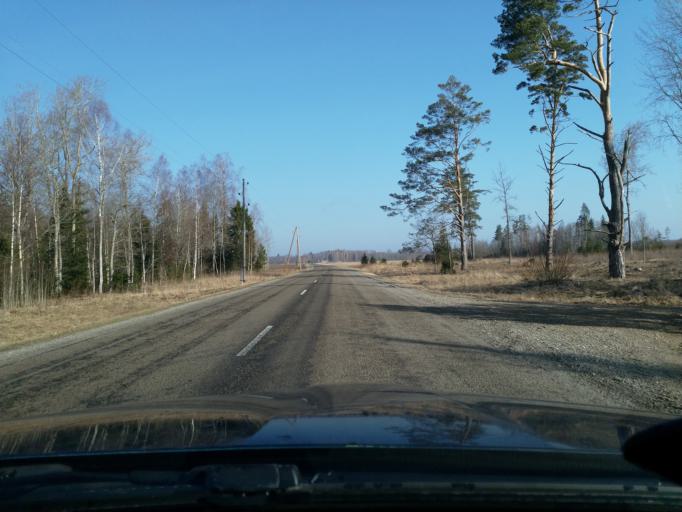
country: LV
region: Kuldigas Rajons
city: Kuldiga
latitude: 56.8729
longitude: 21.9391
